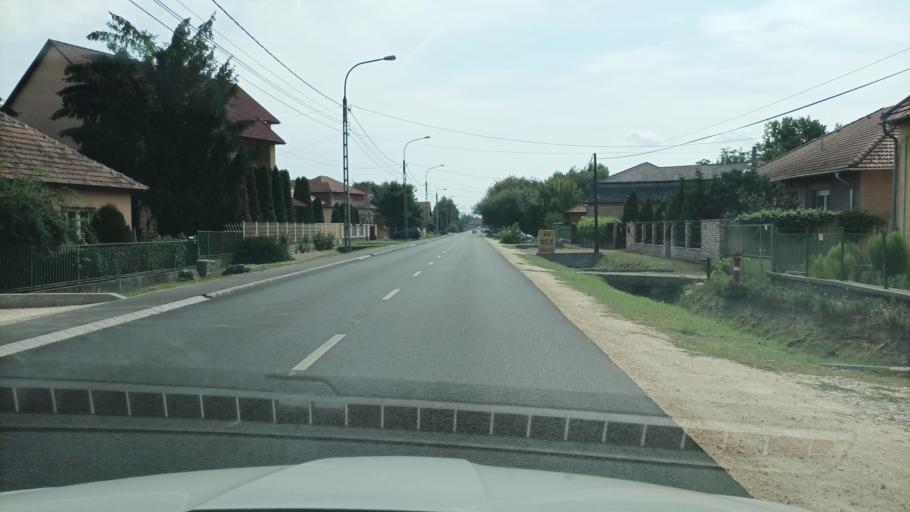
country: HU
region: Pest
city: Tura
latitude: 47.6201
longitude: 19.5976
